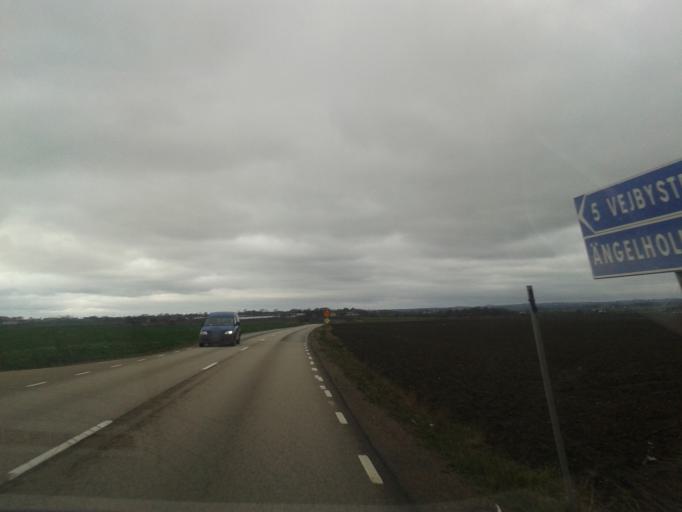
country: SE
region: Skane
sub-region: Bastads Kommun
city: Forslov
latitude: 56.2963
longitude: 12.8304
